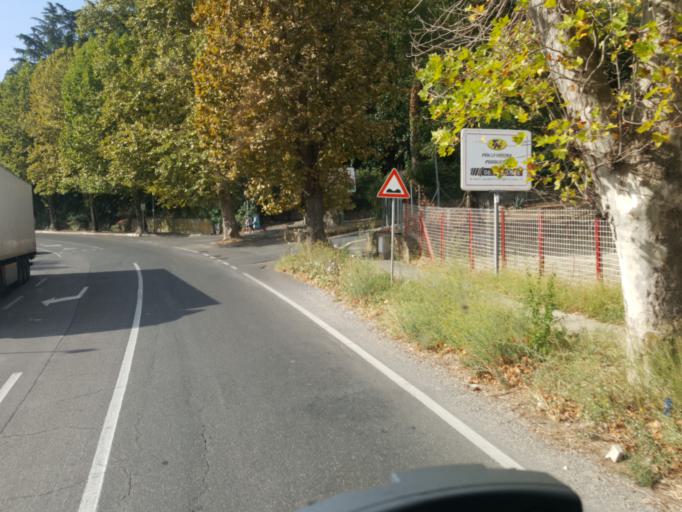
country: IT
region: Latium
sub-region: Citta metropolitana di Roma Capitale
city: Girardi-Bellavista-Terrazze
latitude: 42.1054
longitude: 12.5827
